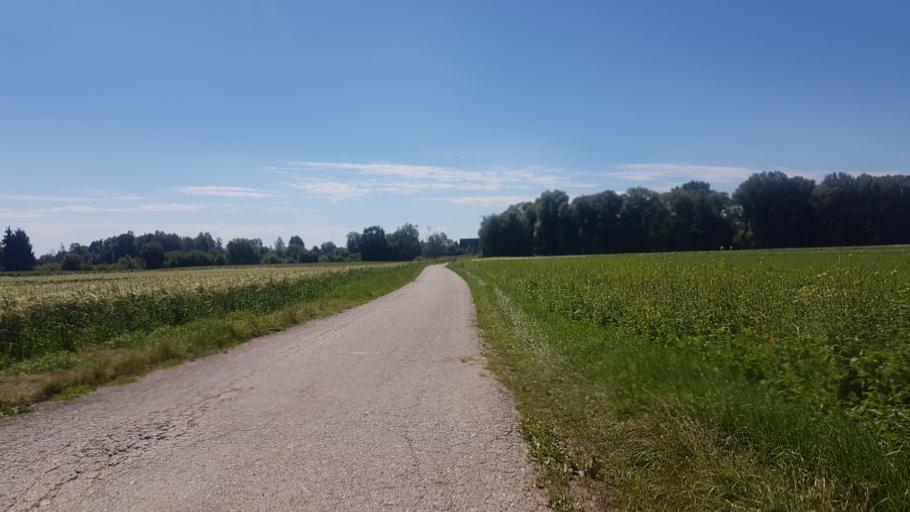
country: DE
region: Bavaria
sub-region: Upper Bavaria
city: Weichering
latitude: 48.7235
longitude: 11.3128
